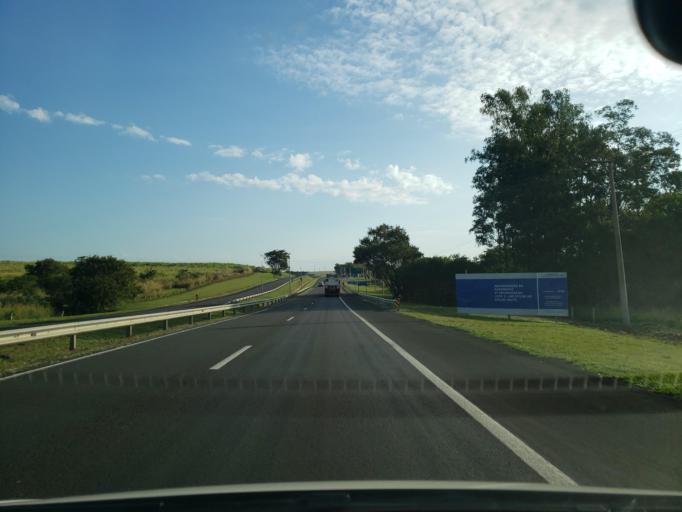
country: BR
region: Sao Paulo
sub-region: Valparaiso
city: Valparaiso
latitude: -21.2108
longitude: -50.8268
